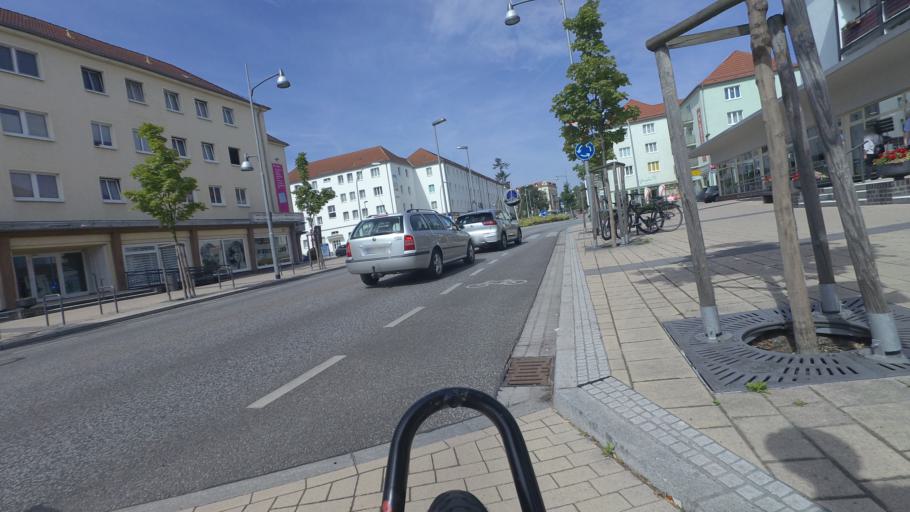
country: DE
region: Brandenburg
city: Rathenow
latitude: 52.6063
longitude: 12.3391
